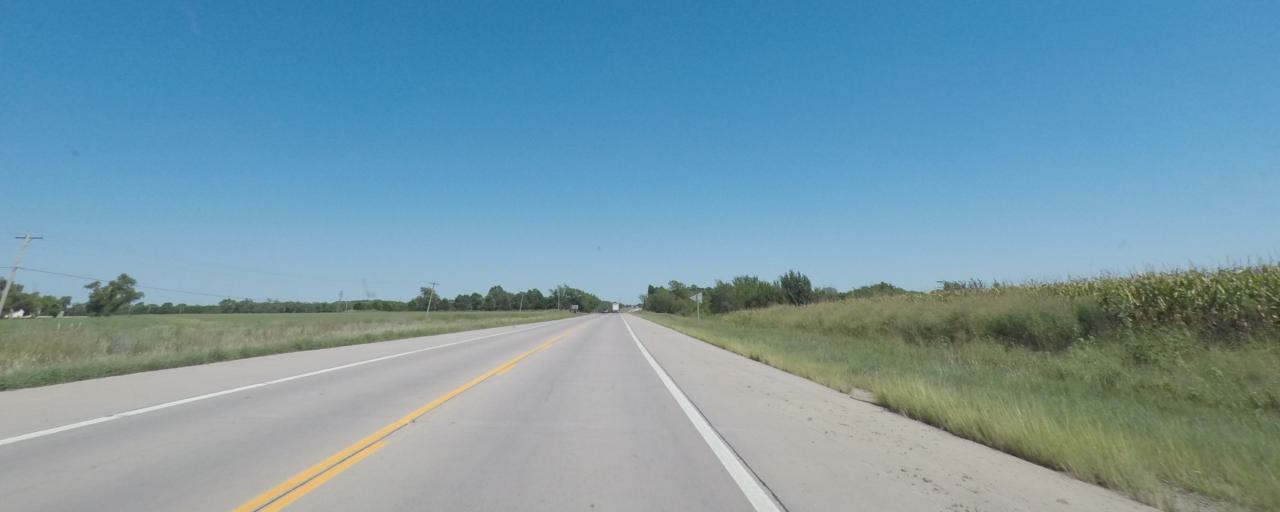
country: US
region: Kansas
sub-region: Lyon County
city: Emporia
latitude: 38.4121
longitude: -96.2779
